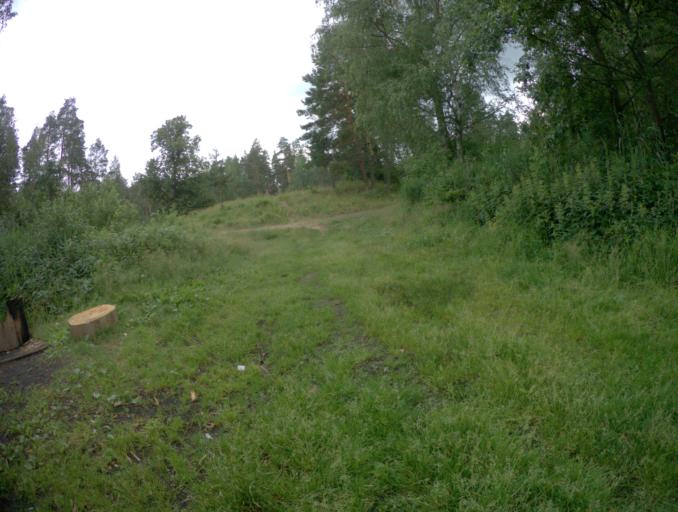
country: RU
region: Vladimir
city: Gorokhovets
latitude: 56.2645
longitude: 42.6782
